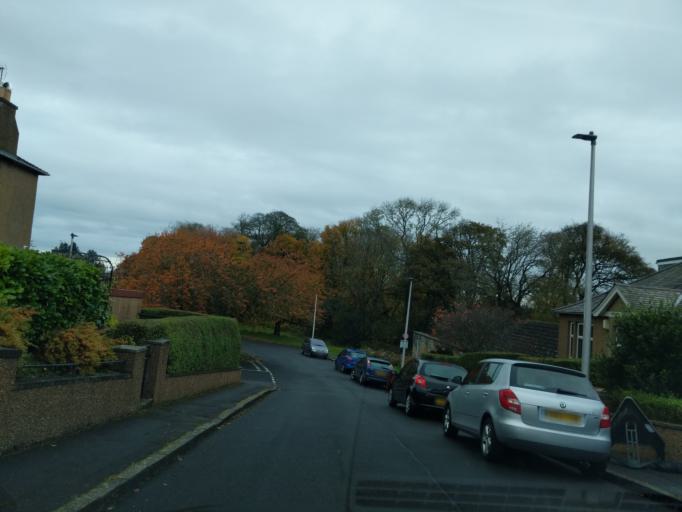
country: GB
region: Scotland
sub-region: Edinburgh
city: Colinton
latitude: 55.9115
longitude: -3.2614
